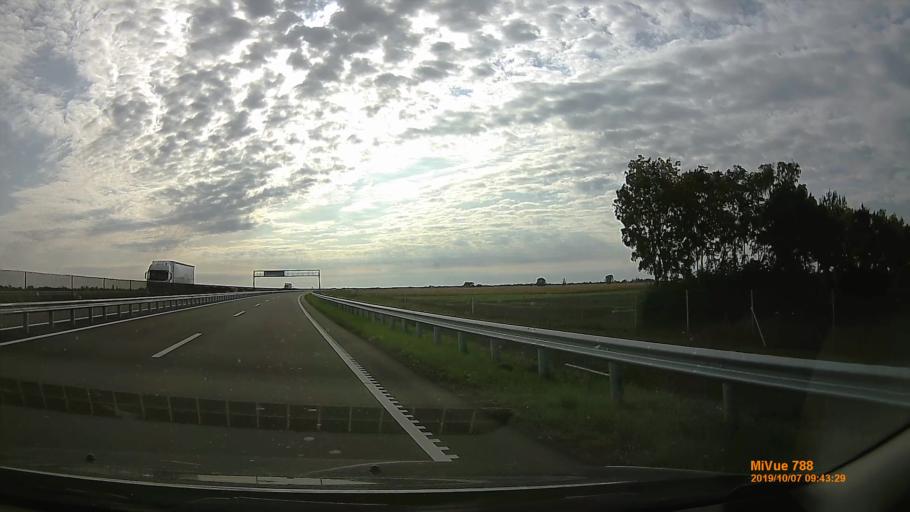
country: HU
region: Bekes
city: Kondoros
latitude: 46.8058
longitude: 20.6902
